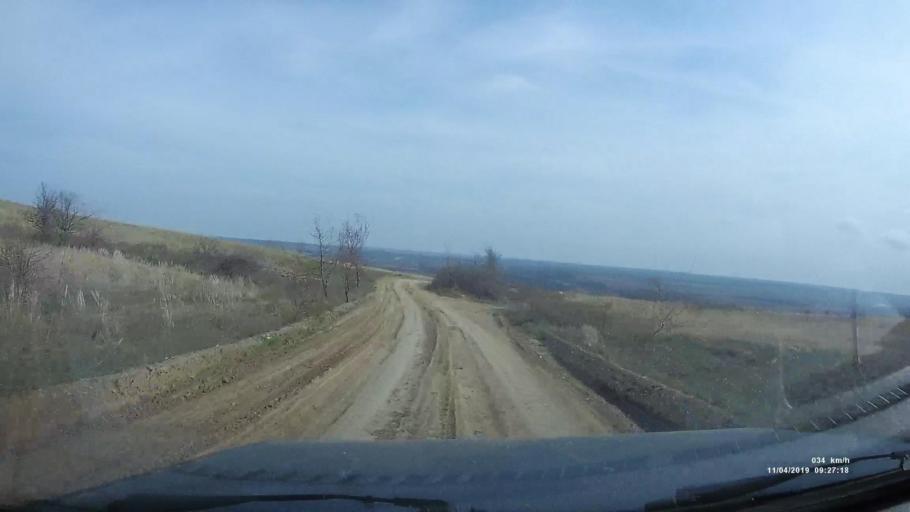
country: RU
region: Rostov
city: Staraya Stanitsa
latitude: 48.2658
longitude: 40.3665
